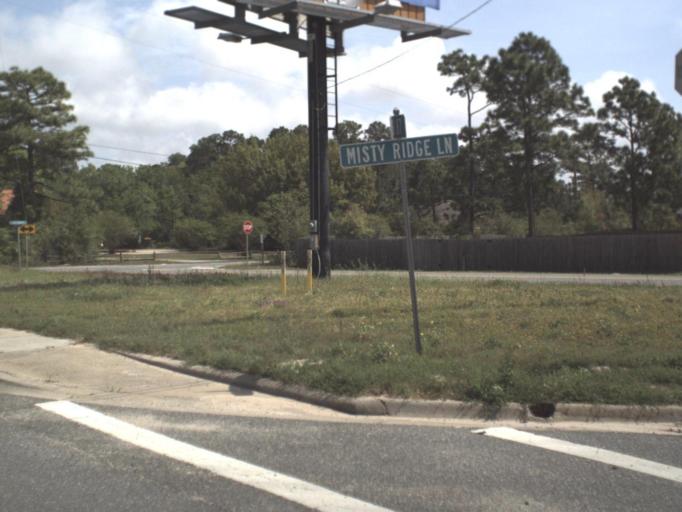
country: US
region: Florida
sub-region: Santa Rosa County
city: Navarre
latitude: 30.4333
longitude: -86.8657
